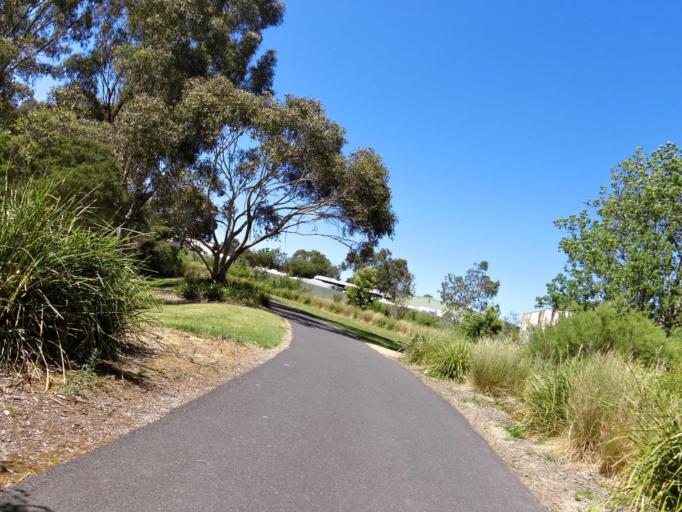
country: AU
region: Victoria
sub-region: Knox
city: Boronia
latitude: -37.8727
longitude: 145.2817
